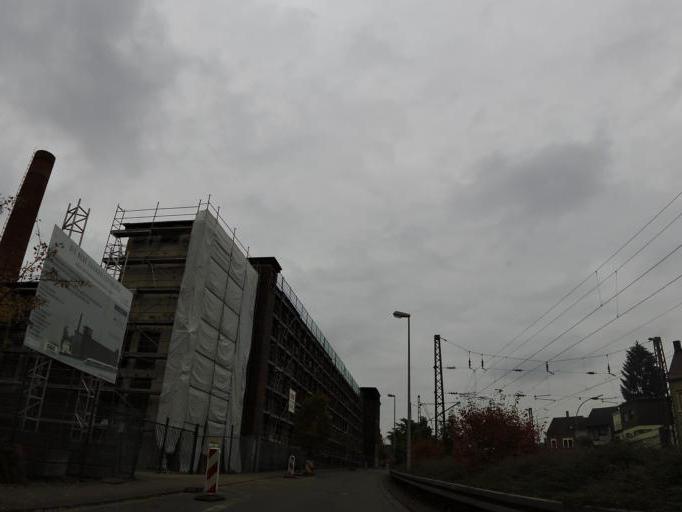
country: DE
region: Saarland
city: Sankt Ingbert
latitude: 49.2763
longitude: 7.1150
